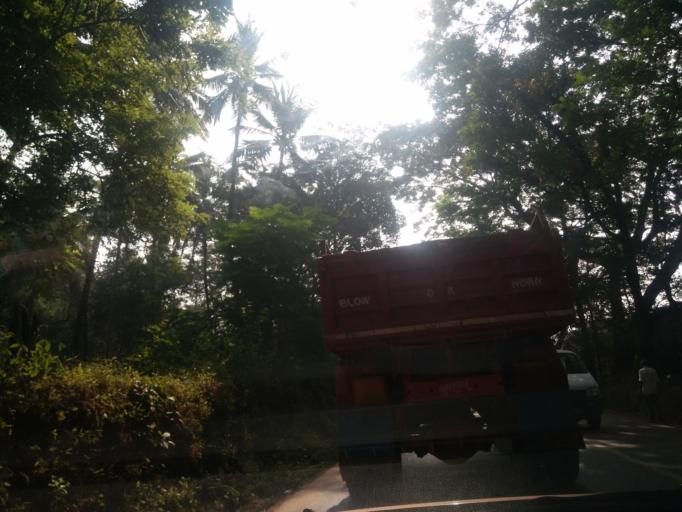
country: IN
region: Goa
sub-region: North Goa
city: Curti
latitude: 15.4222
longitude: 74.0517
